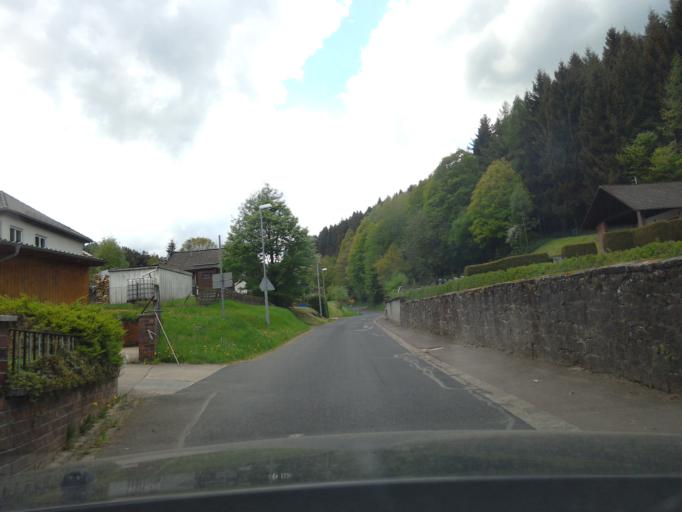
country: DE
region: Bavaria
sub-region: Regierungsbezirk Unterfranken
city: Frammersbach
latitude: 50.1112
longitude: 9.4382
